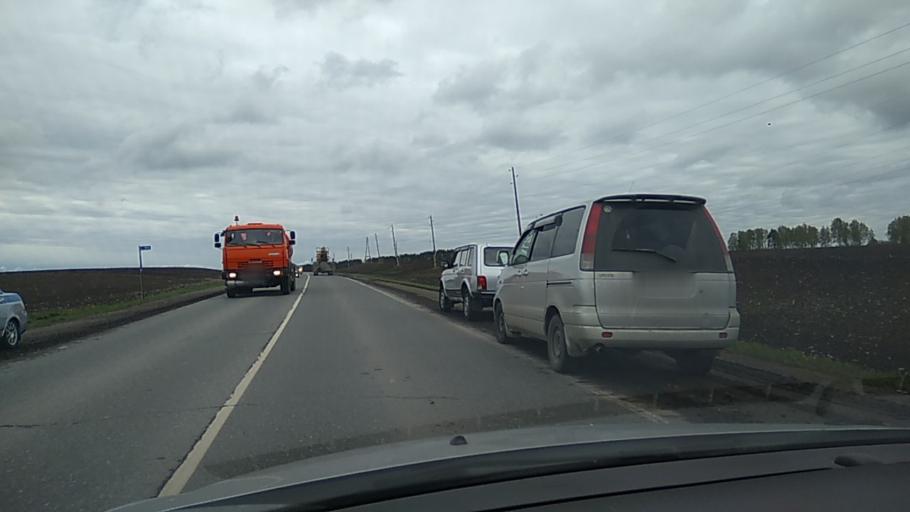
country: RU
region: Tjumen
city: Chervishevo
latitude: 56.8991
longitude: 65.4014
